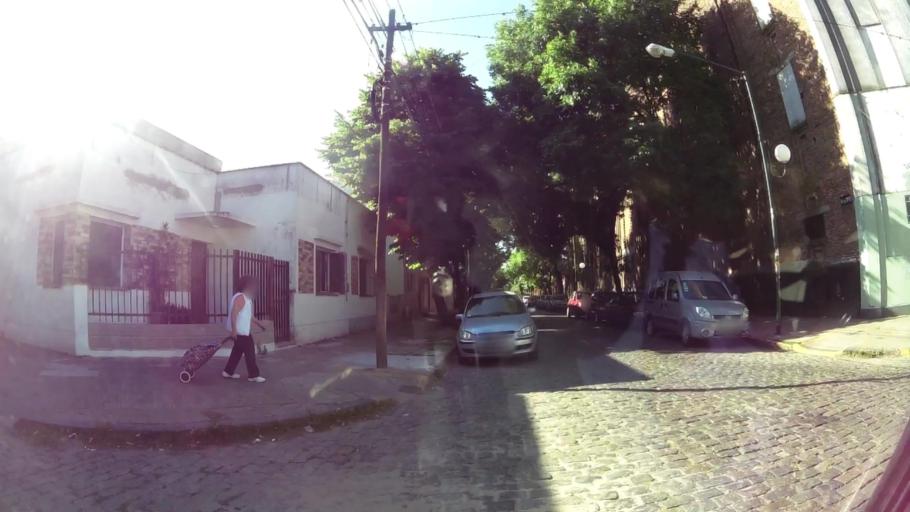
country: AR
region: Buenos Aires
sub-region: Partido de San Isidro
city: San Isidro
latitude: -34.4726
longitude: -58.5201
